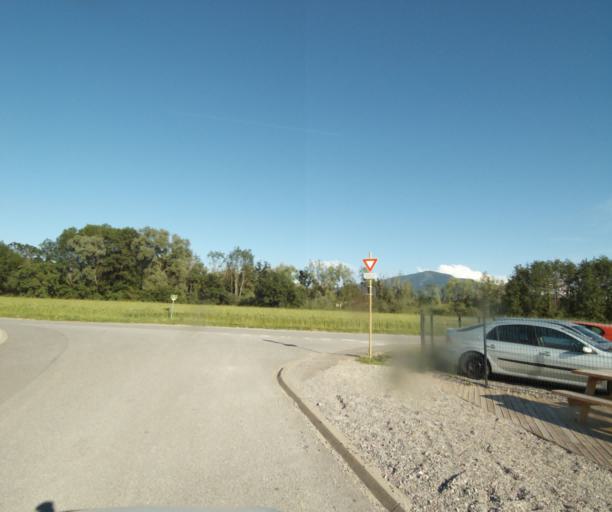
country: FR
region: Rhone-Alpes
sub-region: Departement de la Haute-Savoie
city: Loisin
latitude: 46.2951
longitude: 6.3032
